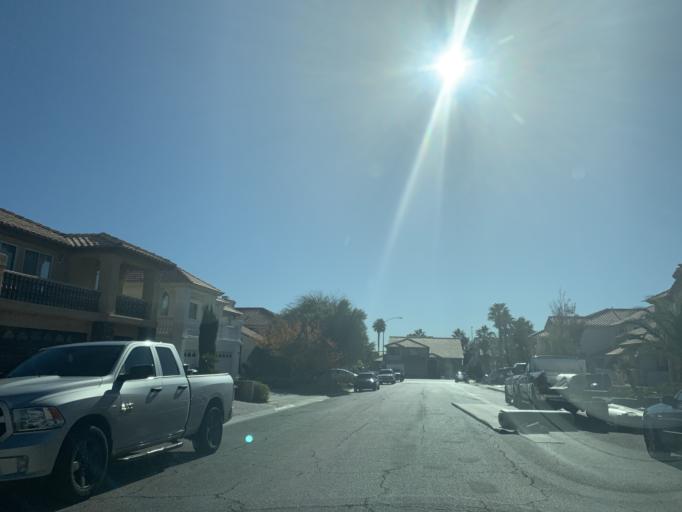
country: US
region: Nevada
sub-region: Clark County
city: Summerlin South
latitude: 36.1218
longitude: -115.2886
